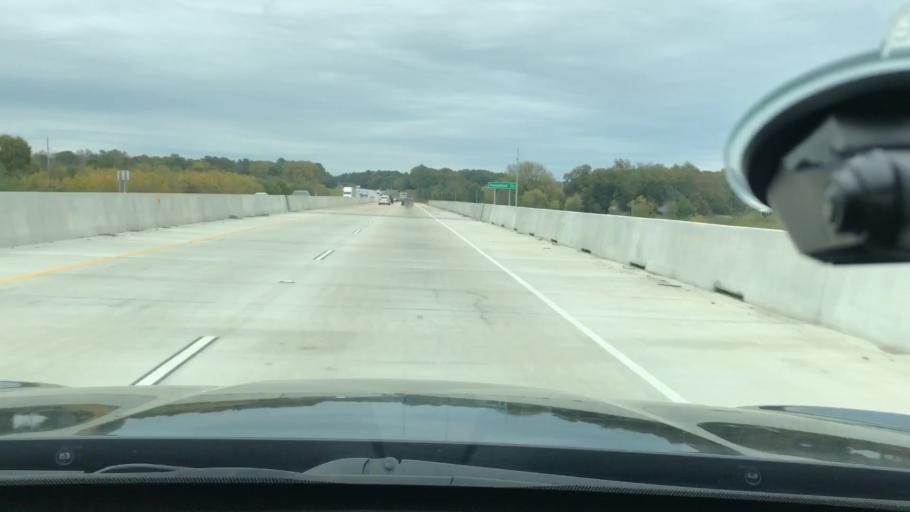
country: US
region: Arkansas
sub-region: Hempstead County
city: Hope
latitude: 33.6060
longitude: -93.8118
